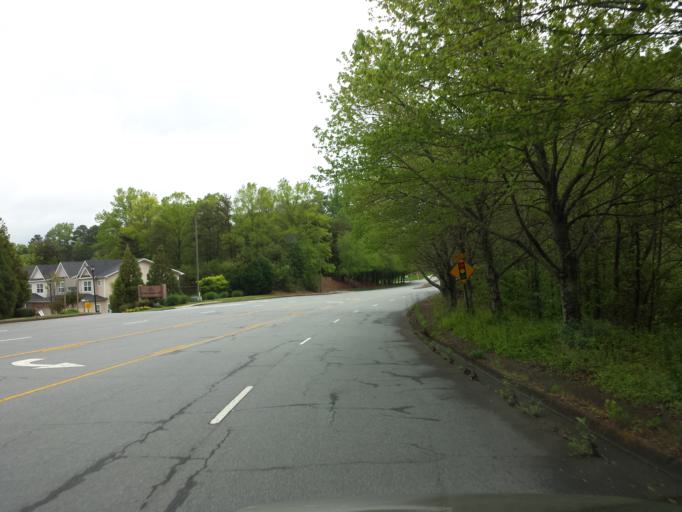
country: US
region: Georgia
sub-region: Cobb County
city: Kennesaw
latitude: 34.0019
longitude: -84.5864
